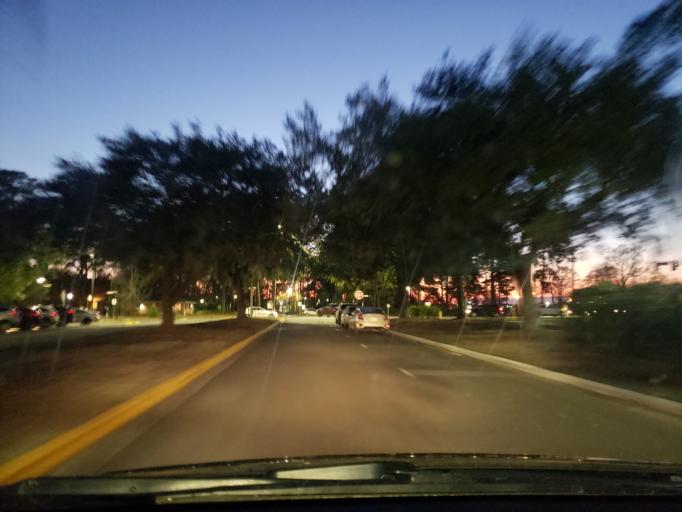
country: US
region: Georgia
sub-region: Chatham County
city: Montgomery
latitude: 31.9812
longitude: -81.1638
